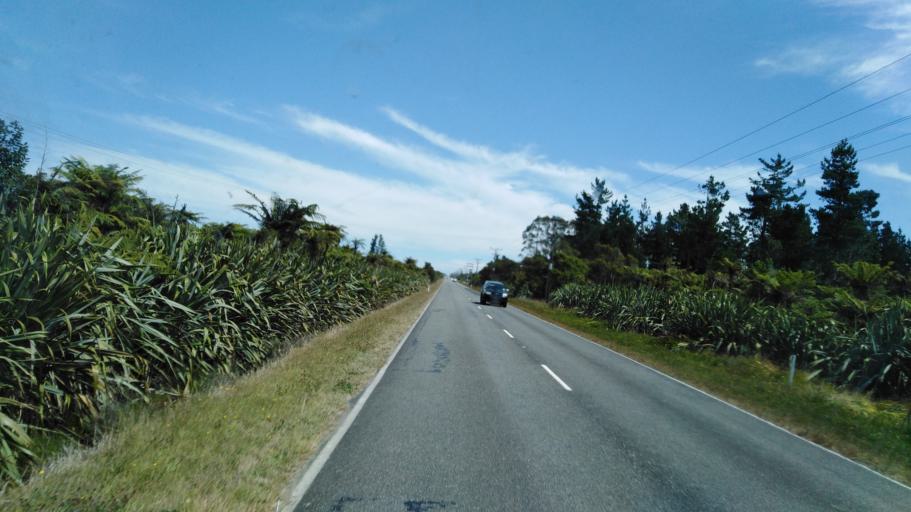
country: NZ
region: West Coast
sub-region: Buller District
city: Westport
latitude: -41.7425
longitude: 171.6925
